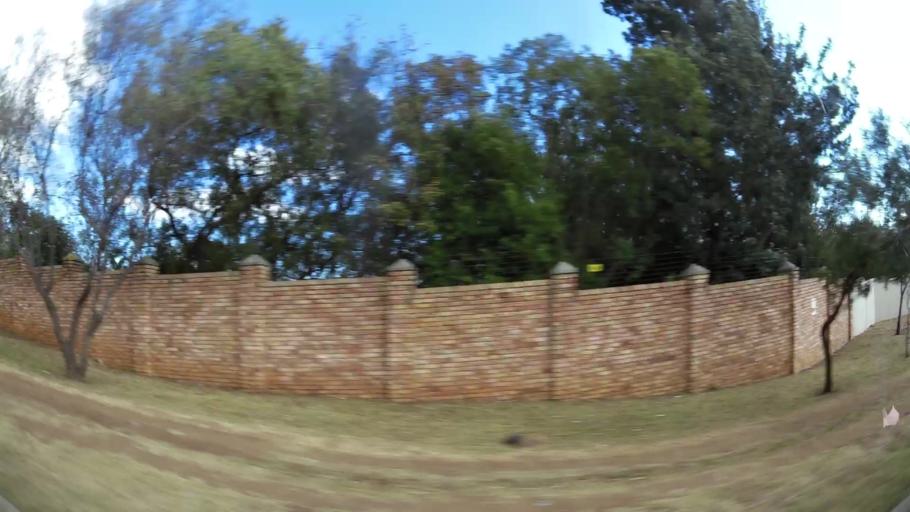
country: ZA
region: Gauteng
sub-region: West Rand District Municipality
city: Muldersdriseloop
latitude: -26.0805
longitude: 27.8564
